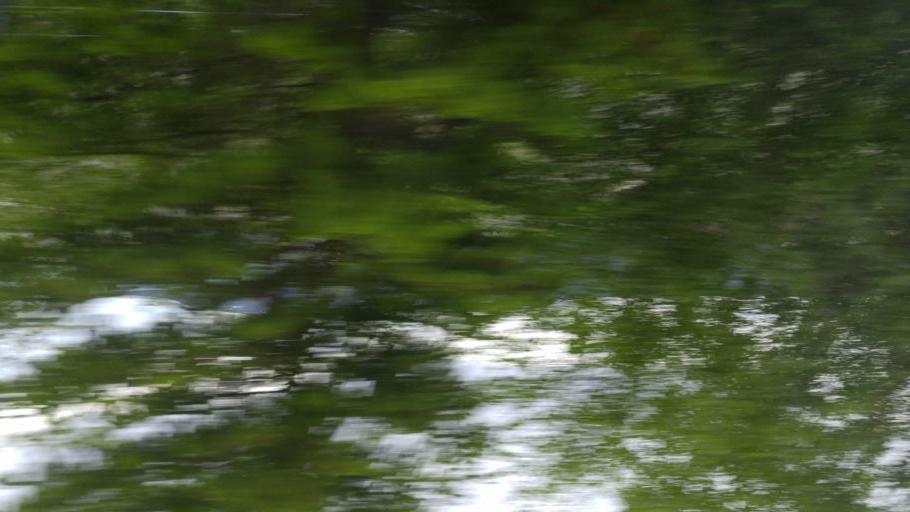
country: NO
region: Nord-Trondelag
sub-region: Meraker
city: Meraker
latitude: 63.3946
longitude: 11.8440
